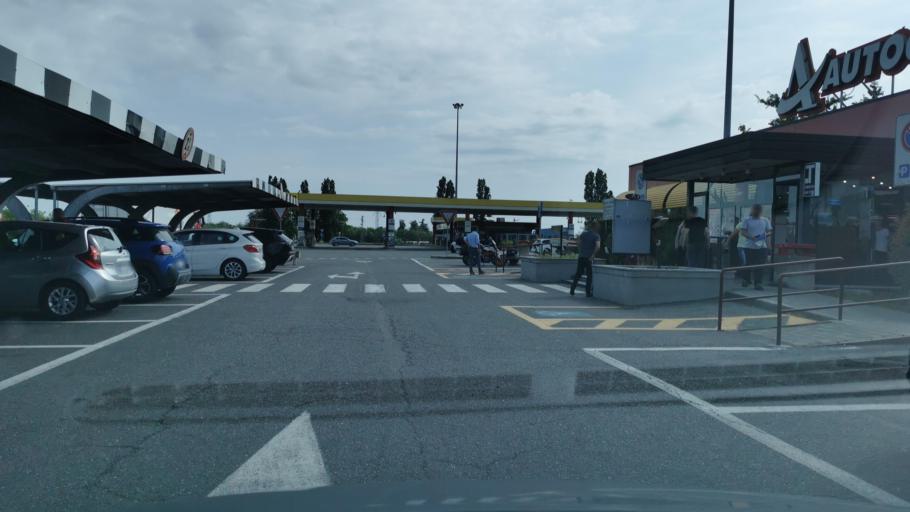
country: IT
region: Piedmont
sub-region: Provincia di Alessandria
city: Tortona
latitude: 44.9346
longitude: 8.8846
